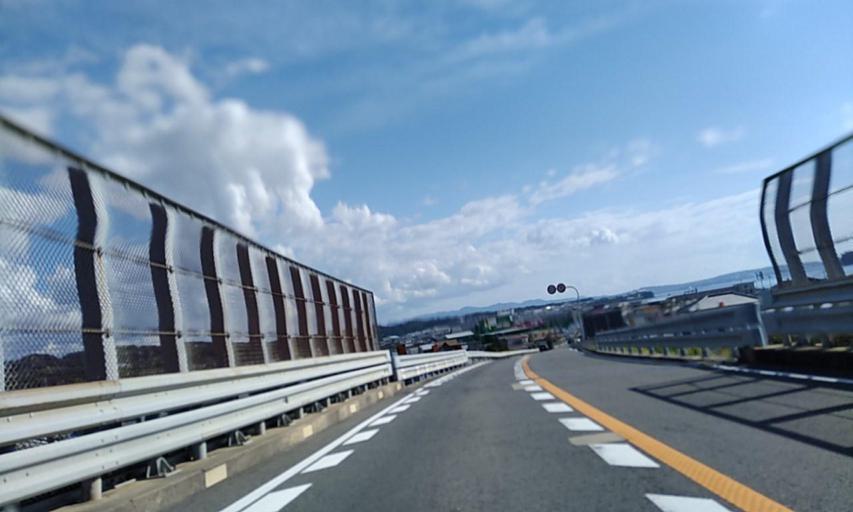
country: JP
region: Wakayama
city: Tanabe
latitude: 33.7760
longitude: 135.3113
